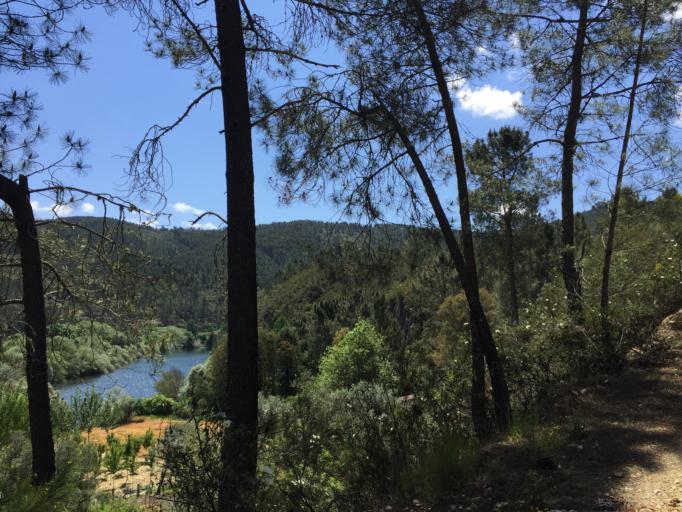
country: PT
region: Coimbra
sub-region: Pampilhosa da Serra
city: Pampilhosa da Serra
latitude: 40.0689
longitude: -7.7778
